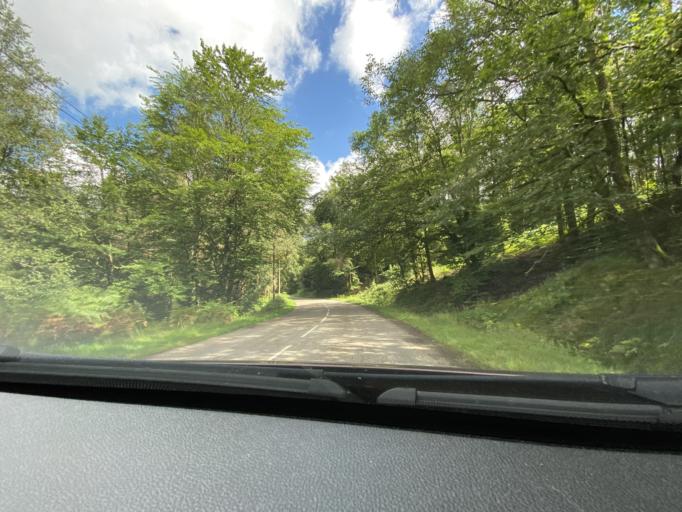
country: FR
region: Bourgogne
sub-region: Departement de la Cote-d'Or
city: Saulieu
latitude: 47.2594
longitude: 4.0733
